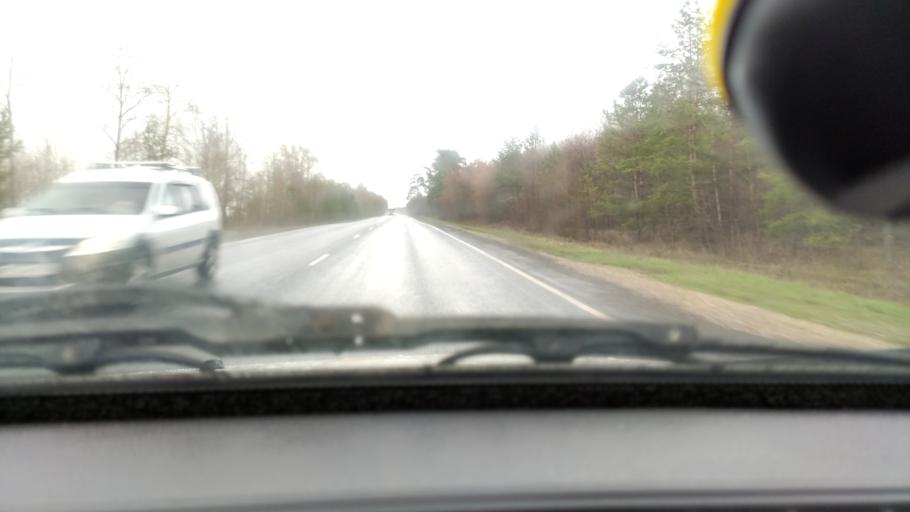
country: RU
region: Samara
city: Povolzhskiy
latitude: 53.6184
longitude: 49.6354
